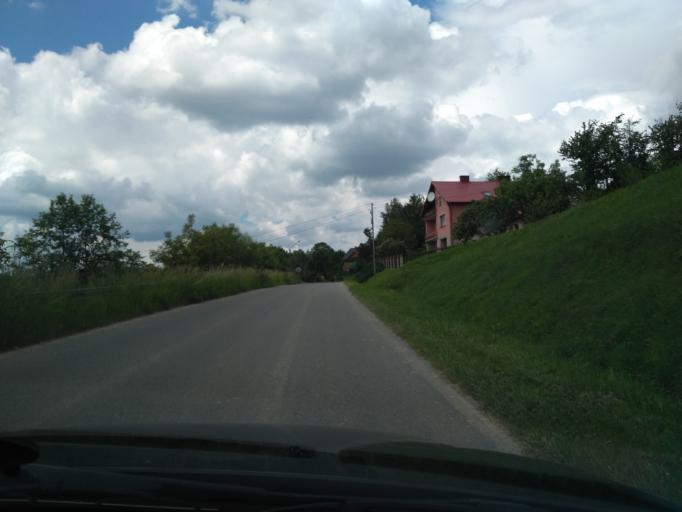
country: PL
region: Subcarpathian Voivodeship
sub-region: Powiat brzozowski
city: Golcowa
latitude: 49.8135
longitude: 22.0488
